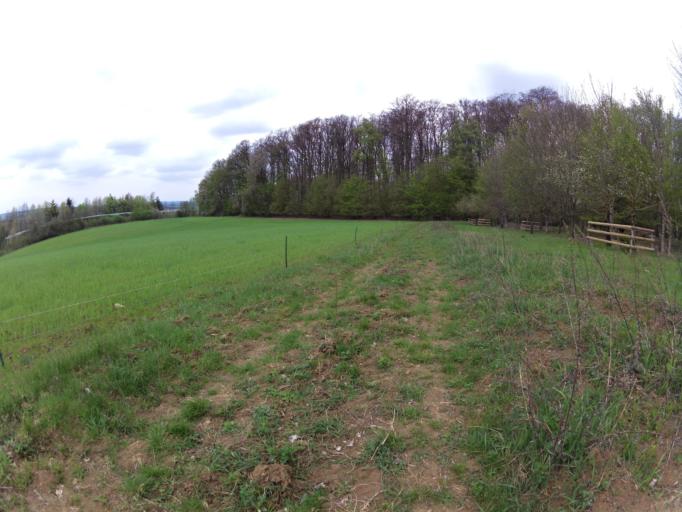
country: DE
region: Bavaria
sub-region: Regierungsbezirk Unterfranken
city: Greussenheim
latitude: 49.8257
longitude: 9.7957
